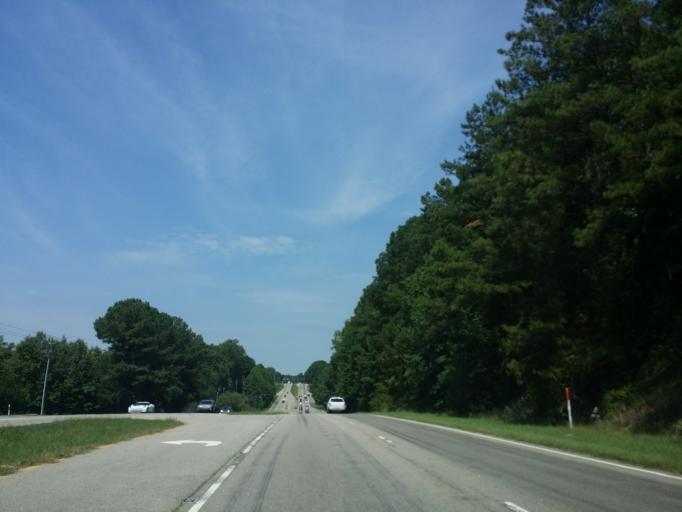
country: US
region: North Carolina
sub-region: Wake County
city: Cary
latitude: 35.8686
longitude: -78.7204
